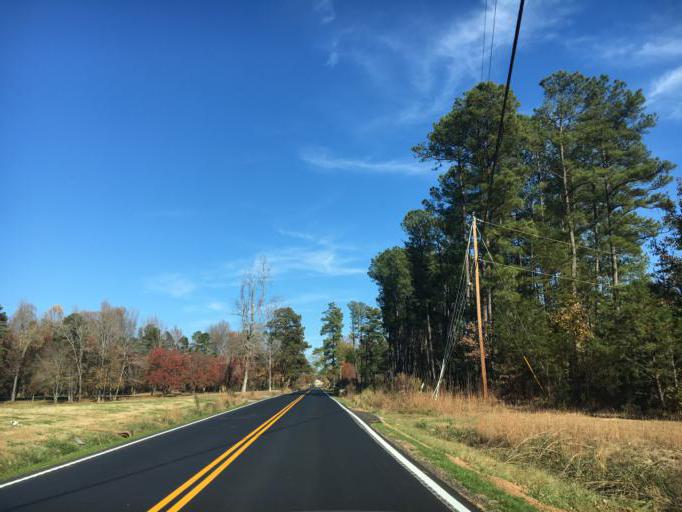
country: US
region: South Carolina
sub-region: Spartanburg County
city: Wellford
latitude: 34.9925
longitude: -82.0676
